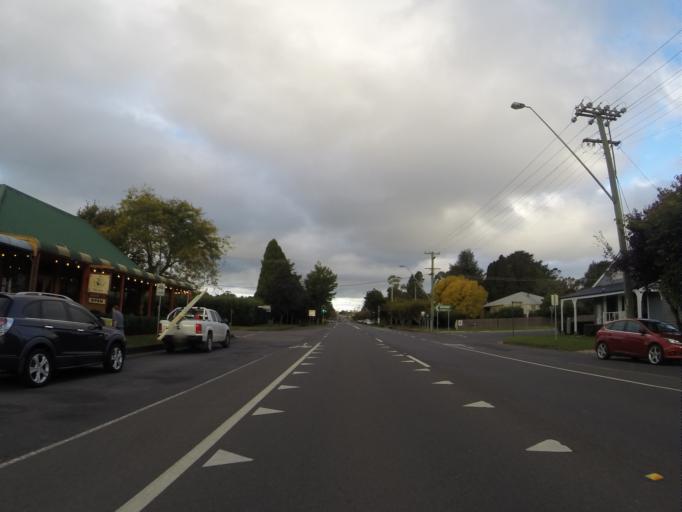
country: AU
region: New South Wales
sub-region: Shellharbour
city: Calderwood
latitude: -34.5884
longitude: 150.5910
